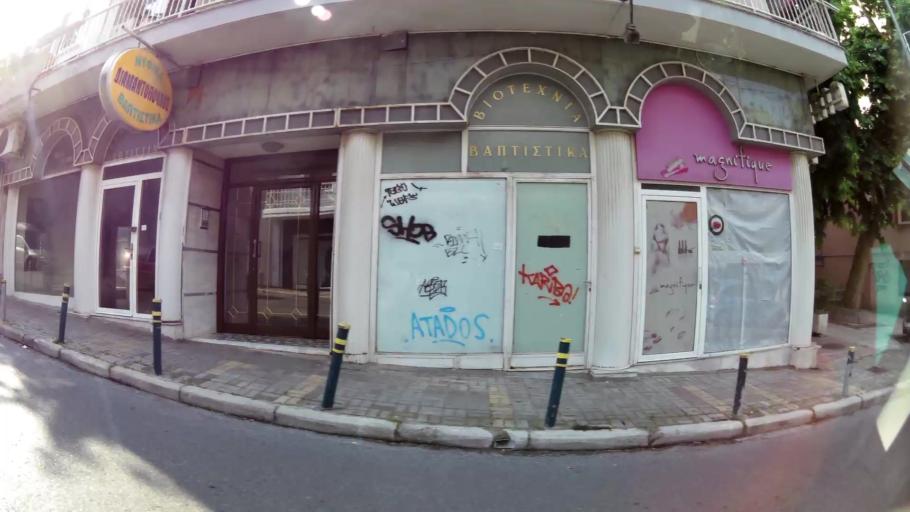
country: GR
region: Central Macedonia
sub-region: Nomos Thessalonikis
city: Sykies
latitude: 40.6461
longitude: 22.9515
